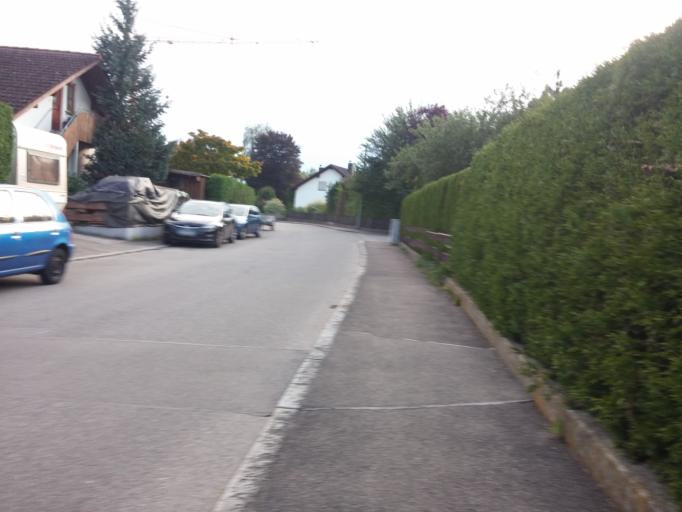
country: DE
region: Bavaria
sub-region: Swabia
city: Buxheim
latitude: 47.9947
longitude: 10.1260
